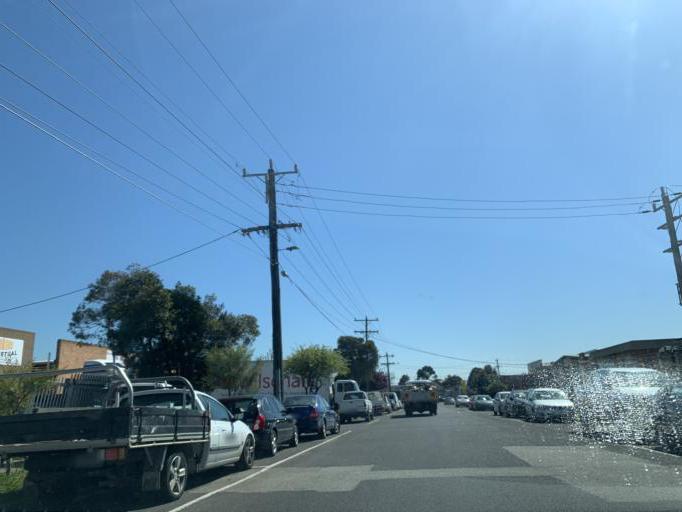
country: AU
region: Victoria
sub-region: Greater Dandenong
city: Dandenong
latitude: -37.9933
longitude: 145.1975
